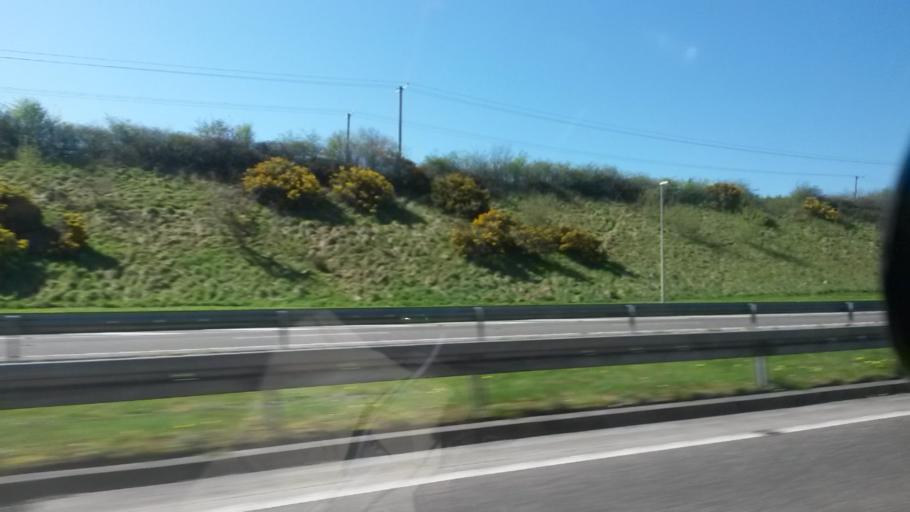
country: IE
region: Munster
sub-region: County Cork
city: Killumney
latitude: 51.8779
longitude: -8.6188
